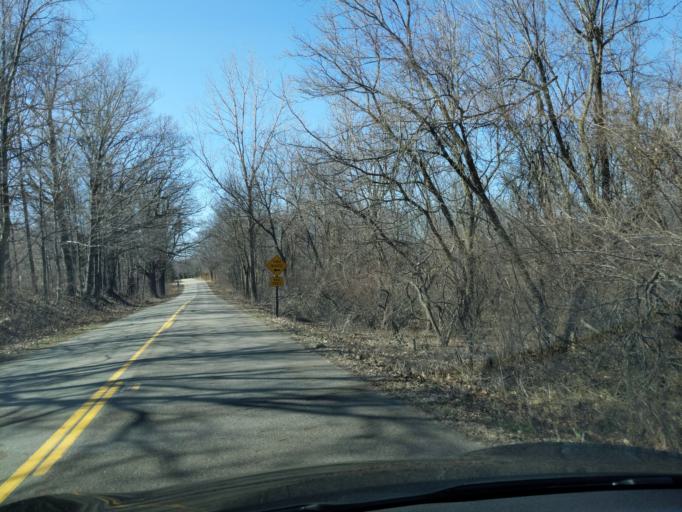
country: US
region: Michigan
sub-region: Ionia County
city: Lake Odessa
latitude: 42.7270
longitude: -85.0513
